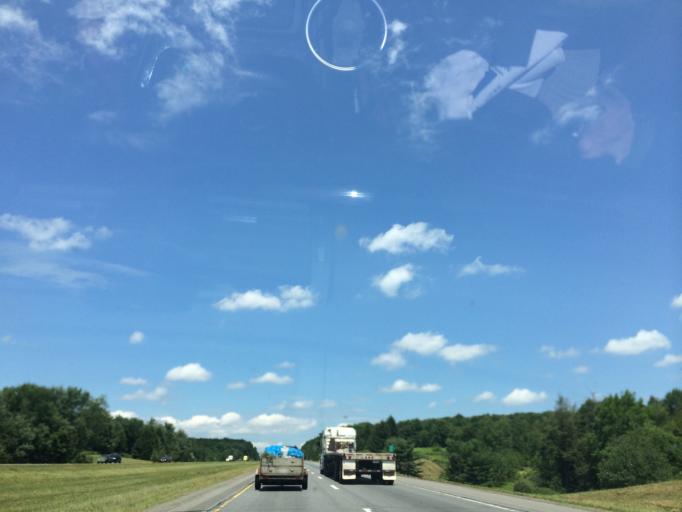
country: US
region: Pennsylvania
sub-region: Lackawanna County
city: Mount Cobb
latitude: 41.3730
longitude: -75.4501
